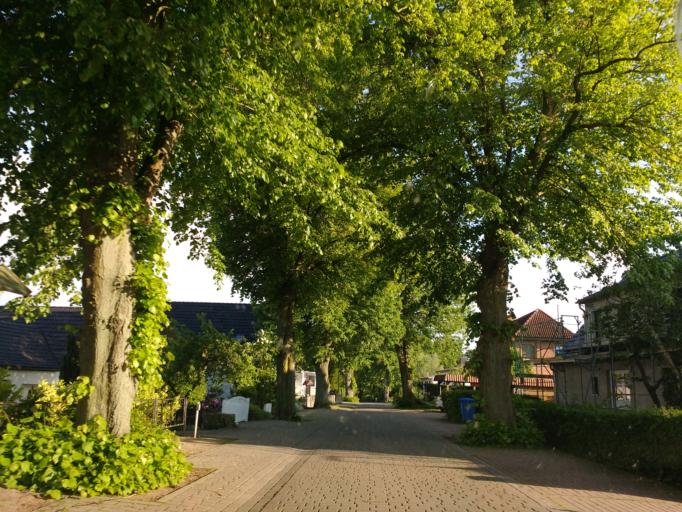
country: DE
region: Mecklenburg-Vorpommern
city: Mecklenburg
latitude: 53.8401
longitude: 11.4702
